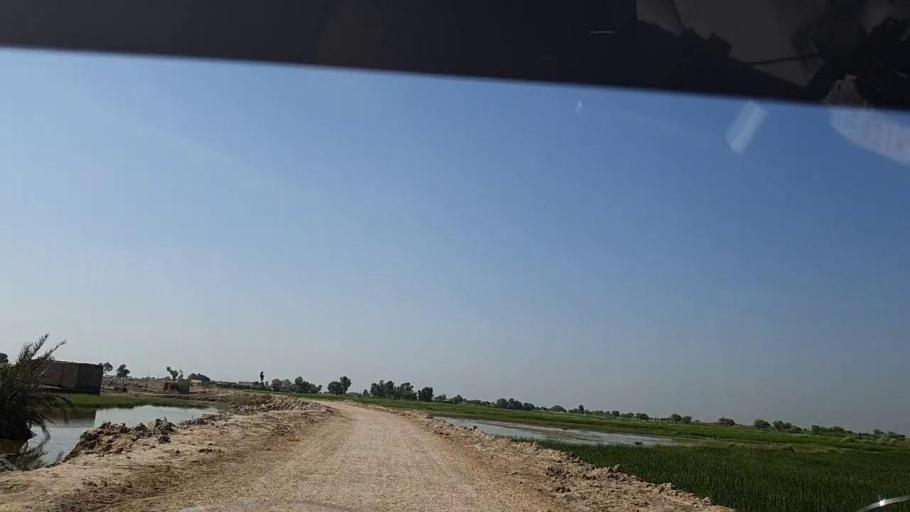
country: PK
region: Sindh
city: Tangwani
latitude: 28.3299
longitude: 69.0763
